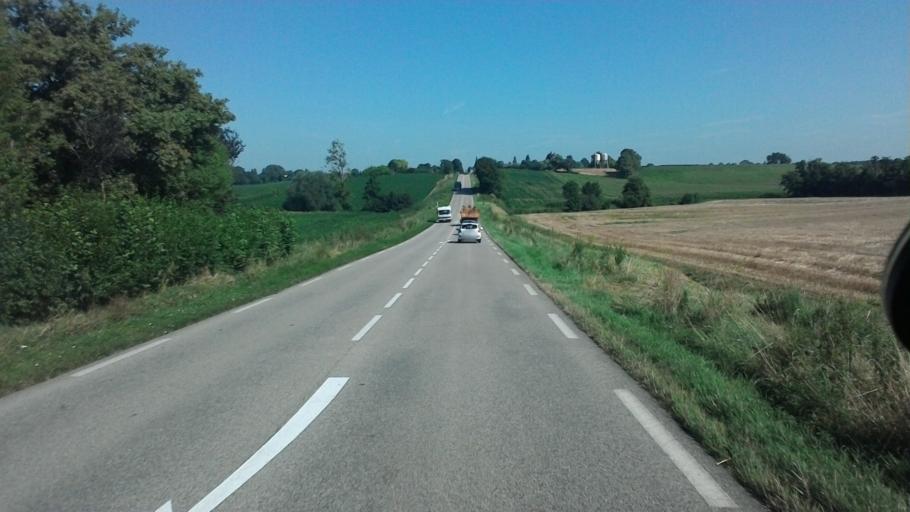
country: FR
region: Rhone-Alpes
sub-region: Departement de l'Ain
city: Saint-Trivier-de-Courtes
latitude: 46.4476
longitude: 5.0881
